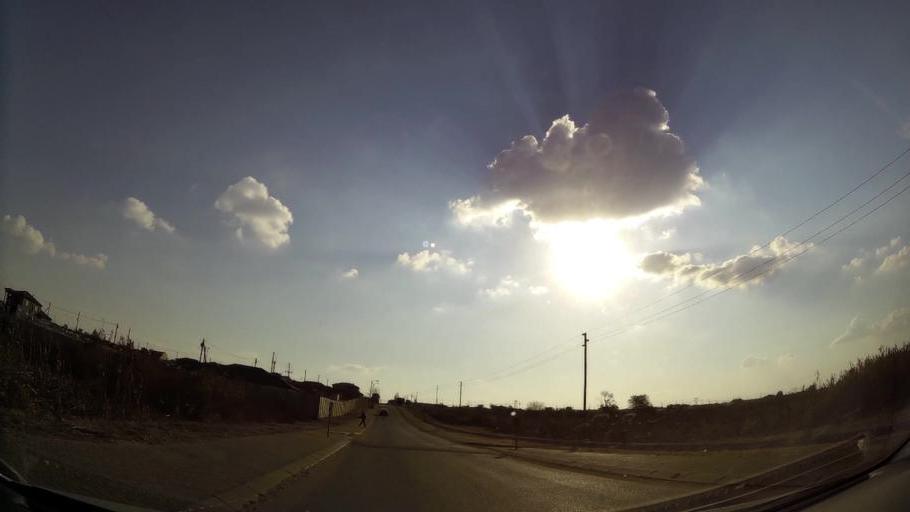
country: ZA
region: Gauteng
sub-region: Ekurhuleni Metropolitan Municipality
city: Tembisa
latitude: -25.9516
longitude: 28.2068
